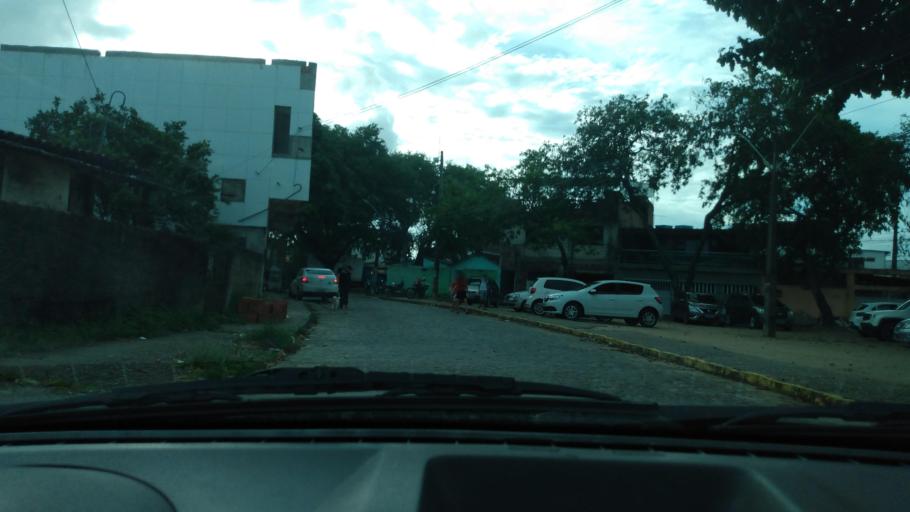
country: BR
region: Pernambuco
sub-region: Jaboatao Dos Guararapes
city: Jaboatao dos Guararapes
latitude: -8.1166
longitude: -34.9482
